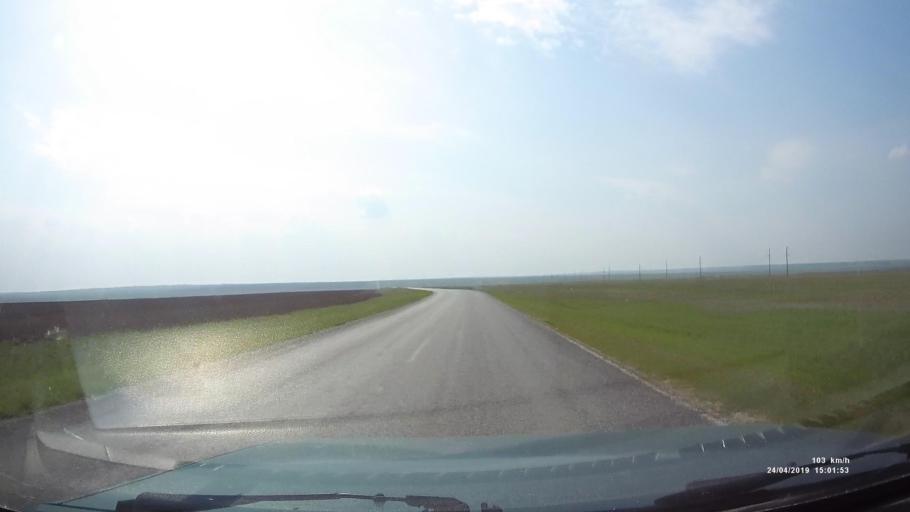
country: RU
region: Rostov
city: Remontnoye
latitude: 46.5666
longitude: 43.5242
